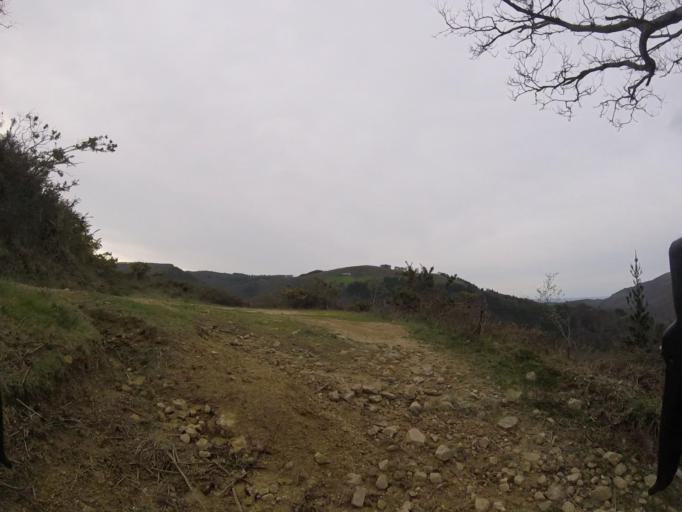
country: ES
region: Navarre
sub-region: Provincia de Navarra
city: Bera
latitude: 43.2895
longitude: -1.7392
